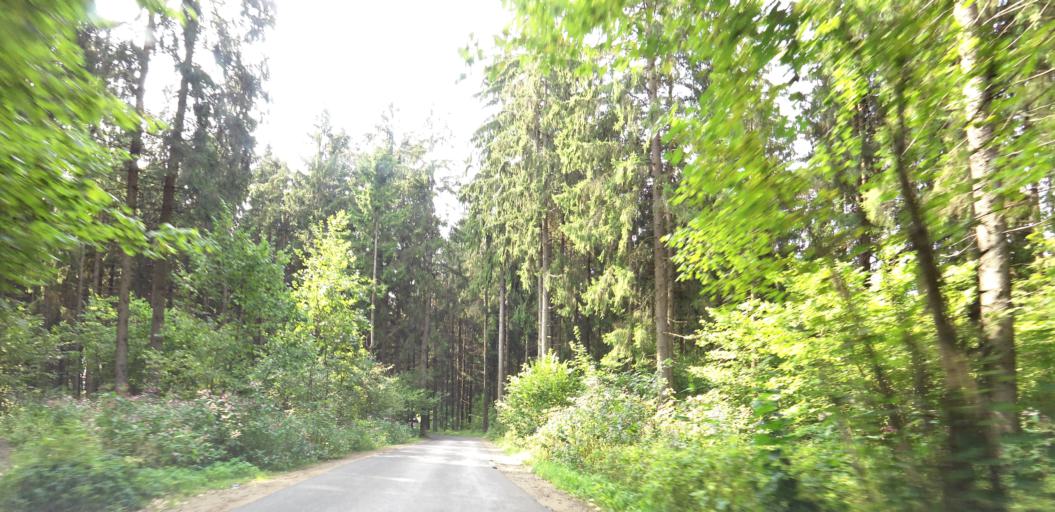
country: LT
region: Vilnius County
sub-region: Vilnius
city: Fabijoniskes
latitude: 54.7436
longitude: 25.2425
